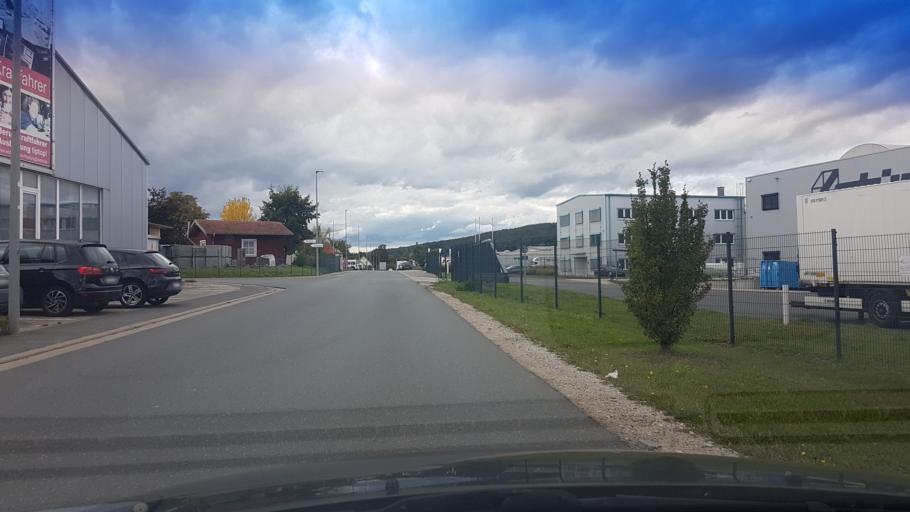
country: DE
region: Bavaria
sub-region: Upper Franconia
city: Pettstadt
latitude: 49.8293
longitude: 10.9393
